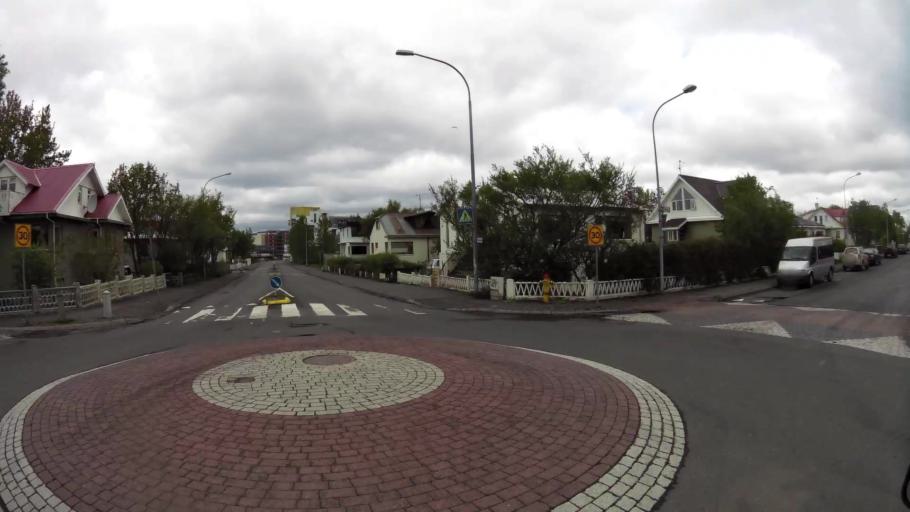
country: IS
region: Capital Region
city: Reykjavik
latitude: 64.1431
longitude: -21.9032
